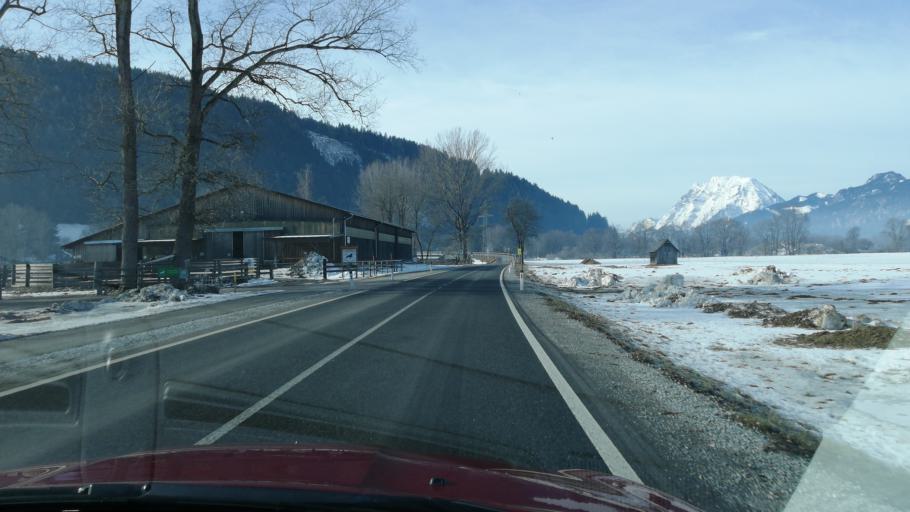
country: AT
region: Styria
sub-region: Politischer Bezirk Liezen
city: Liezen
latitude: 47.5566
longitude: 14.2264
